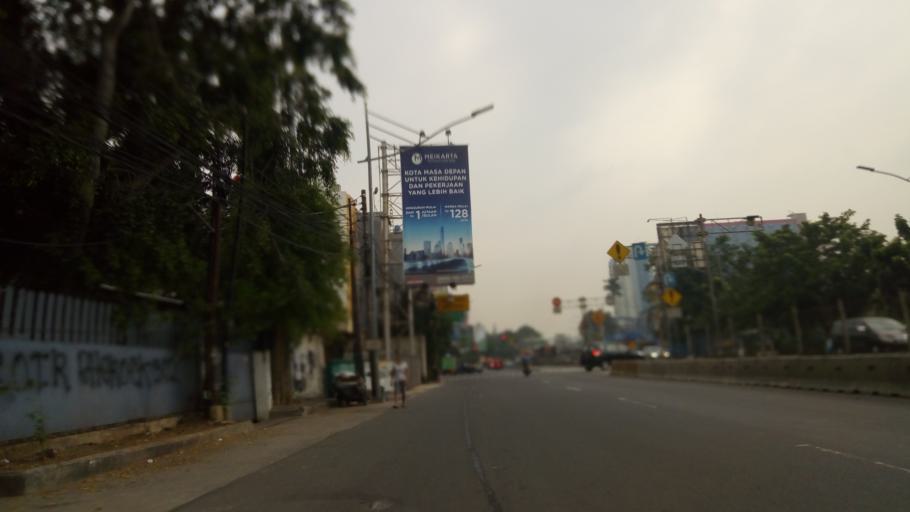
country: ID
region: Jakarta Raya
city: Jakarta
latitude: -6.1439
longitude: 106.8341
